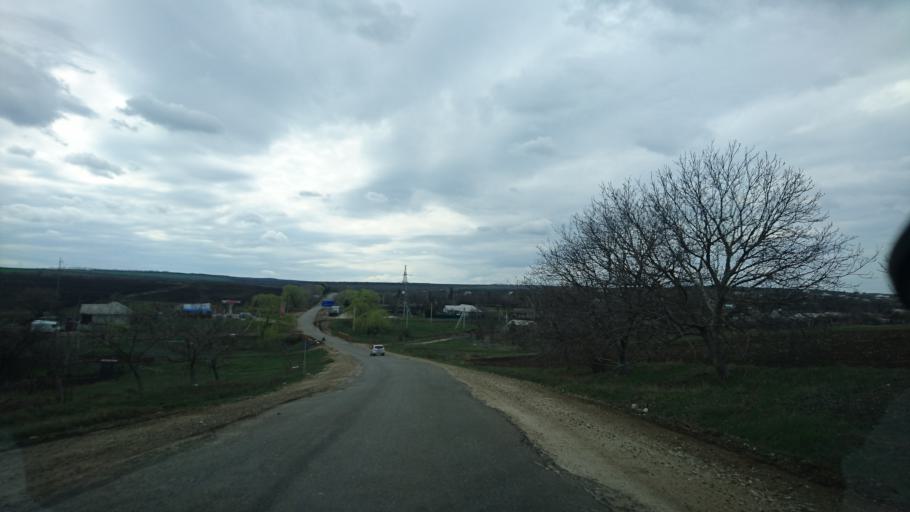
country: MD
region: Gagauzia
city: Comrat
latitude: 46.3106
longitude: 28.5750
